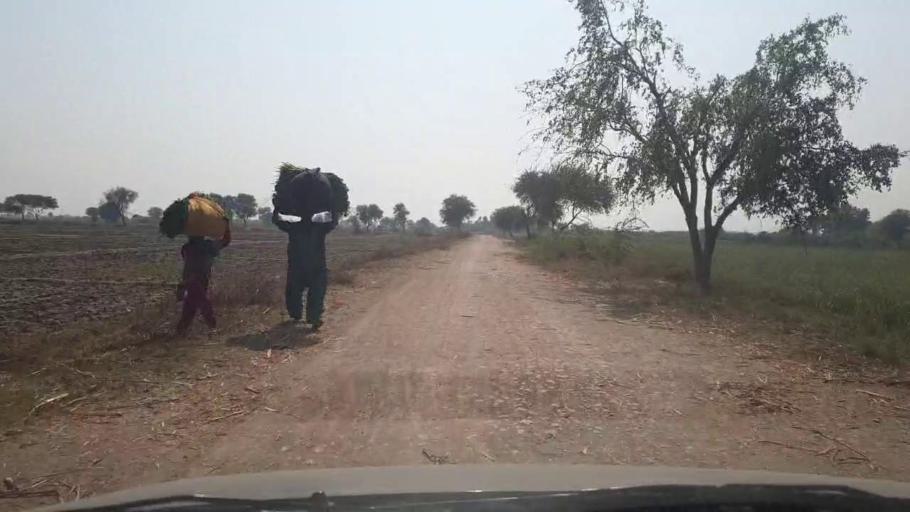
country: PK
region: Sindh
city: Mirwah Gorchani
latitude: 25.3064
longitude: 69.1578
